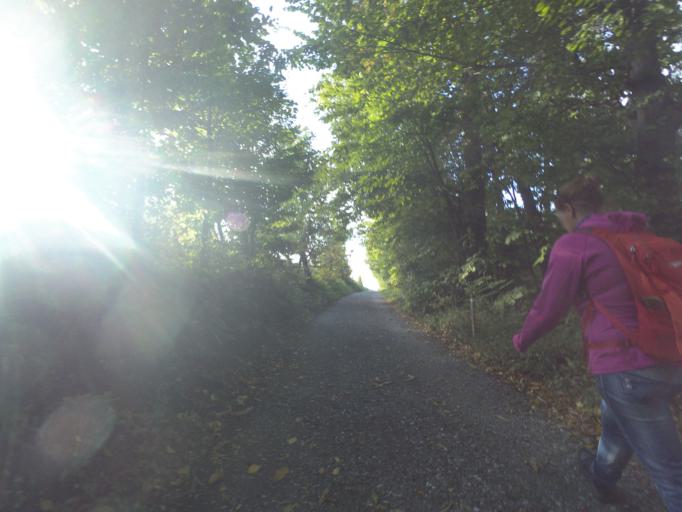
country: AT
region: Styria
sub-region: Politischer Bezirk Leibnitz
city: Kitzeck im Sausal
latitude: 46.7882
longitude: 15.4276
